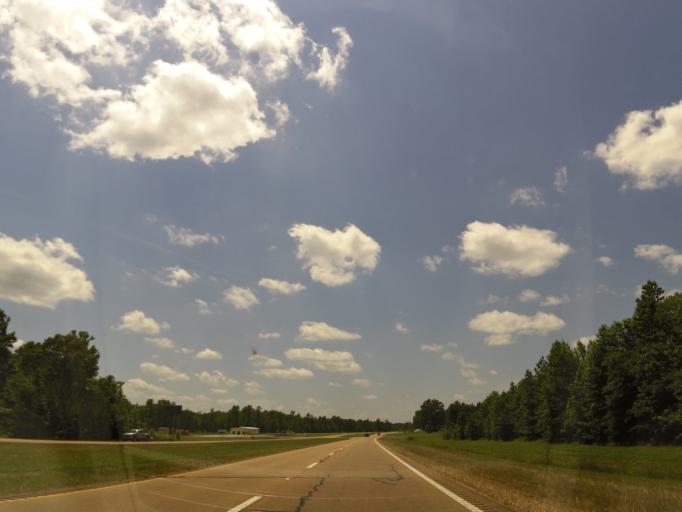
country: US
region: Mississippi
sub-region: Pontotoc County
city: Pontotoc
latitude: 34.2811
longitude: -89.1203
